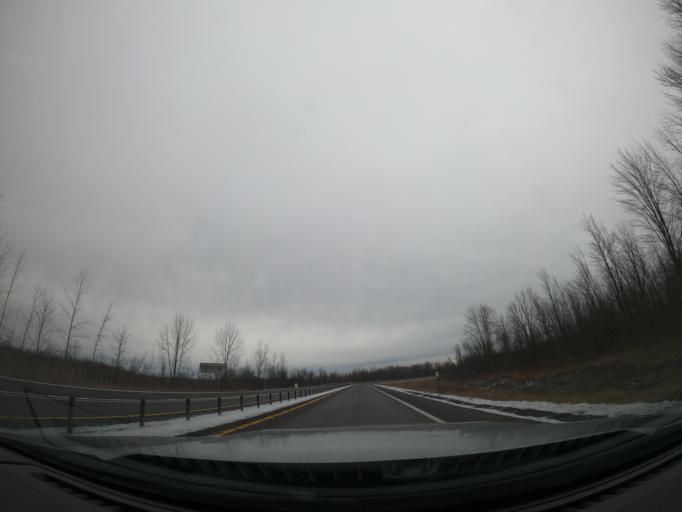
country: US
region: New York
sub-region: Onondaga County
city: East Syracuse
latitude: 43.1066
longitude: -76.0542
